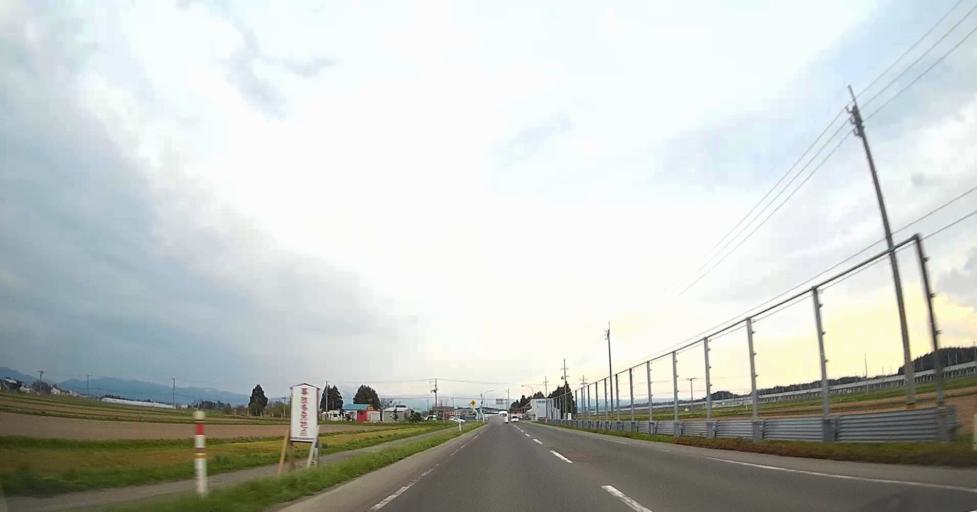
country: JP
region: Aomori
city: Aomori Shi
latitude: 40.8710
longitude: 140.6750
